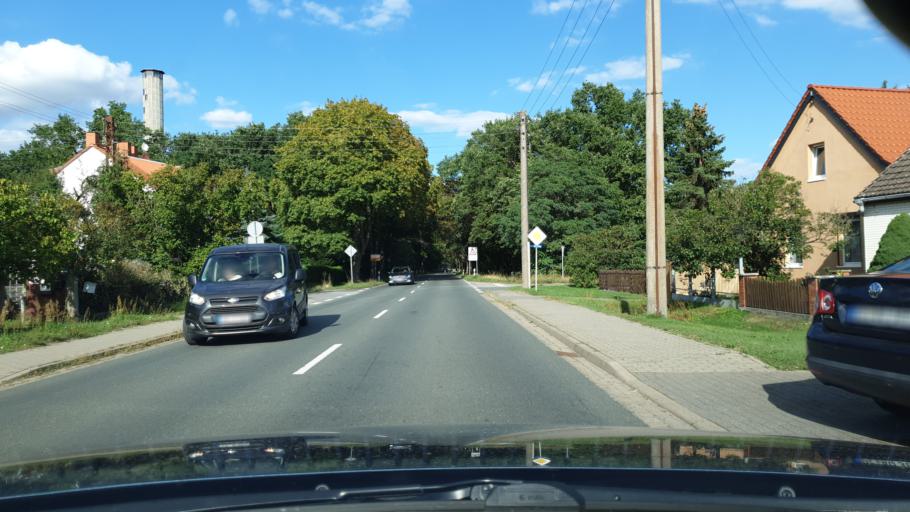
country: DE
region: Saxony-Anhalt
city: Radis
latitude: 51.7554
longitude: 12.5217
